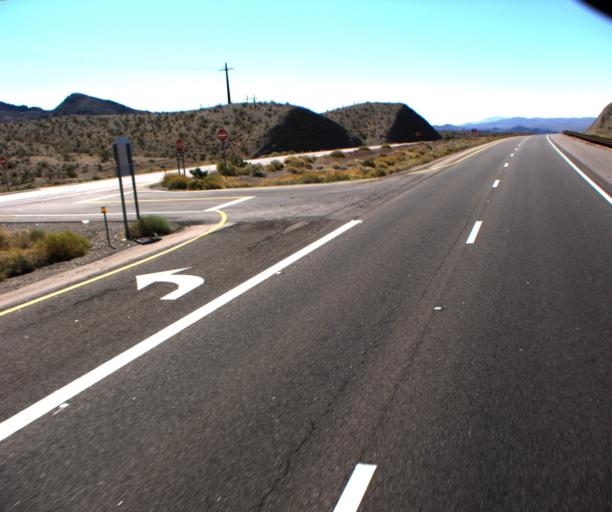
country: US
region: Nevada
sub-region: Clark County
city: Boulder City
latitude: 35.9159
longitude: -114.6299
